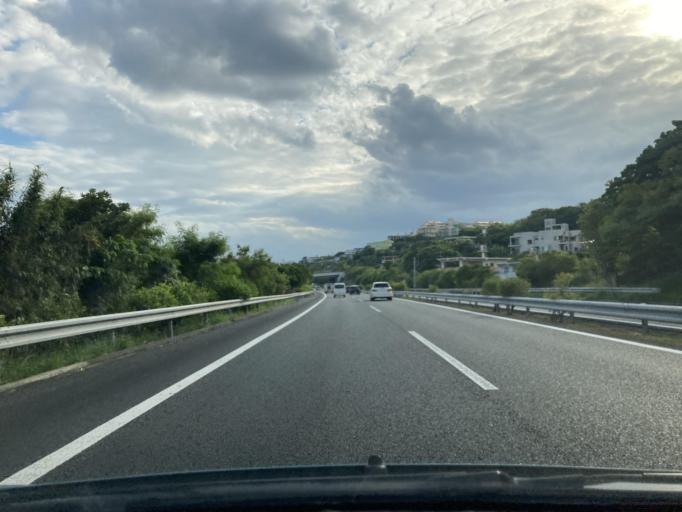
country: JP
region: Okinawa
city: Ginowan
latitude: 26.2710
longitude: 127.7768
